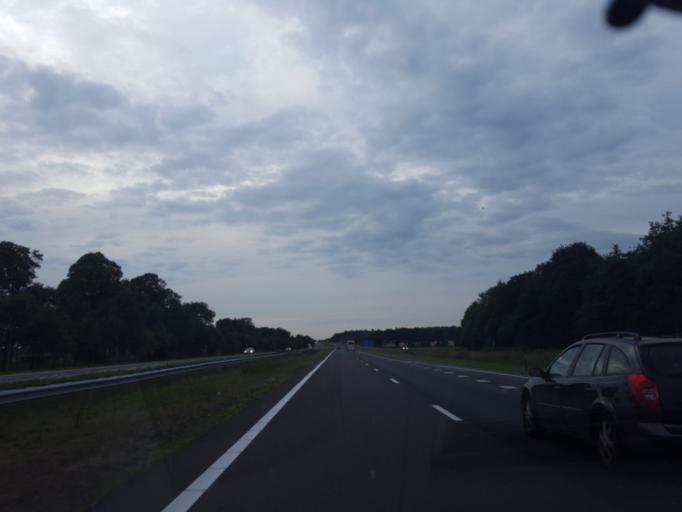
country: NL
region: Drenthe
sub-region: Gemeente Westerveld
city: Havelte
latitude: 52.7570
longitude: 6.1854
